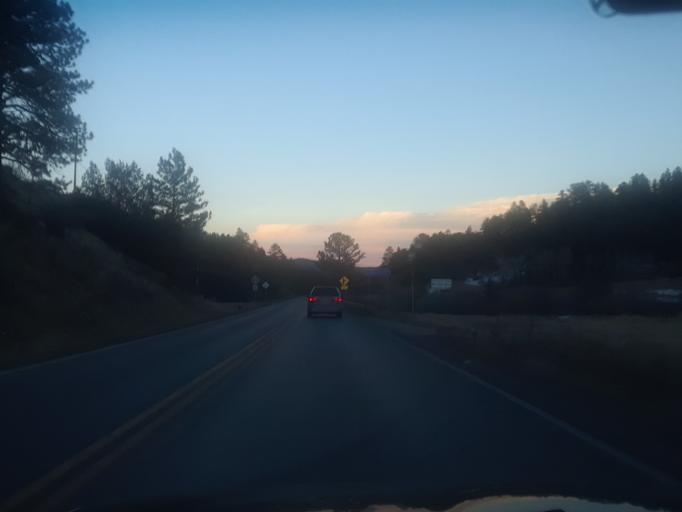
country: US
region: Colorado
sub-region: Jefferson County
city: Evergreen
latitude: 39.4155
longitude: -105.5253
